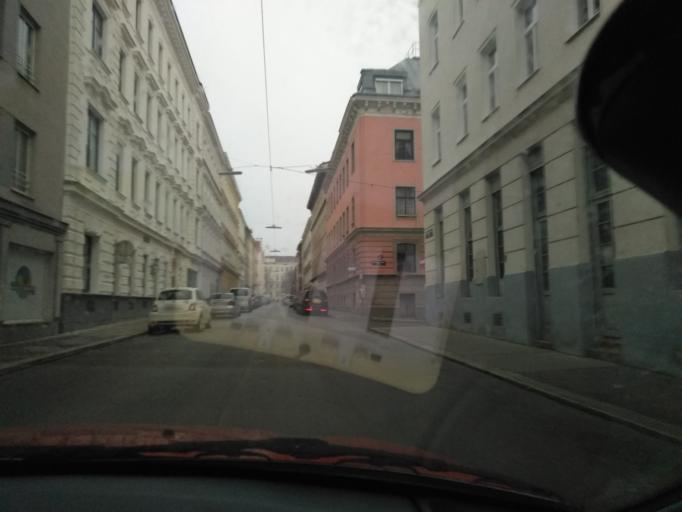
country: AT
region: Vienna
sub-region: Wien Stadt
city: Vienna
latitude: 48.2253
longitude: 16.3374
